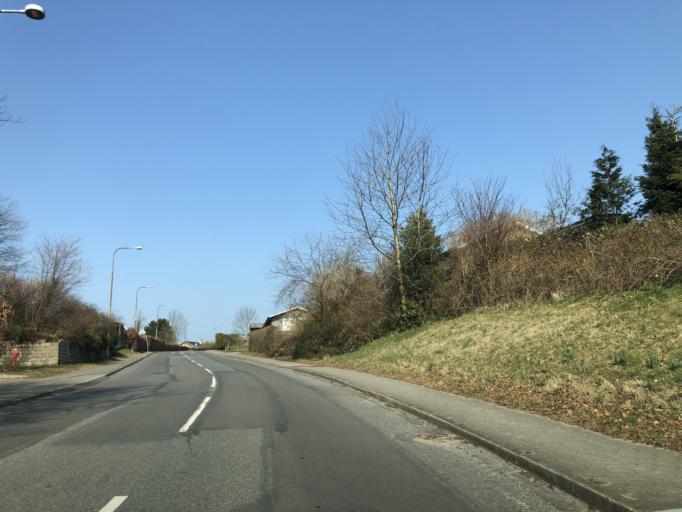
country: DK
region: South Denmark
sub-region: Sonderborg Kommune
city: Nordborg
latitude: 55.0596
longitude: 9.7423
